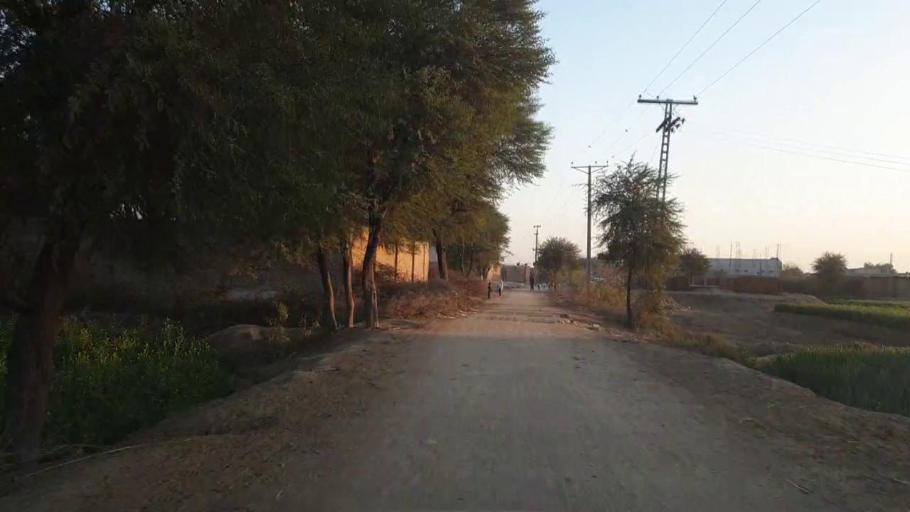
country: PK
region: Sindh
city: Tando Allahyar
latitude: 25.3693
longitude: 68.7471
